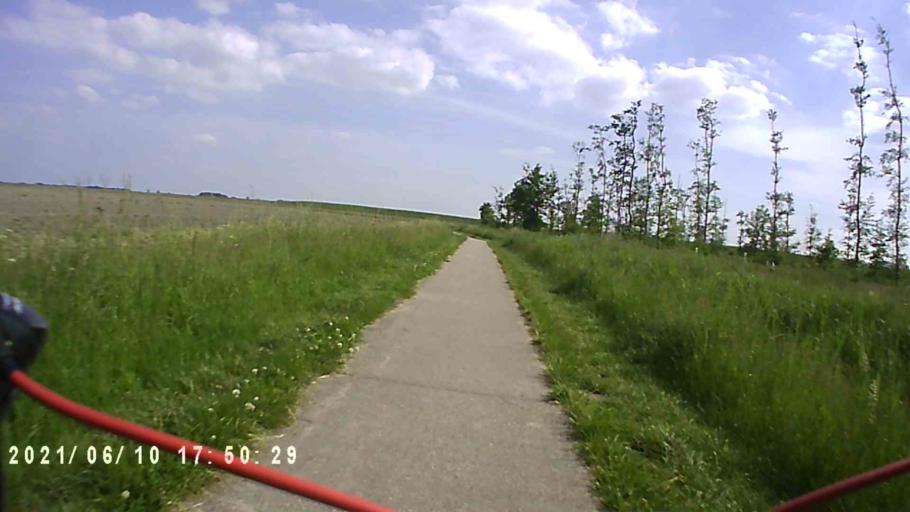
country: NL
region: Groningen
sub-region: Gemeente De Marne
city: Ulrum
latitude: 53.3330
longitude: 6.3125
